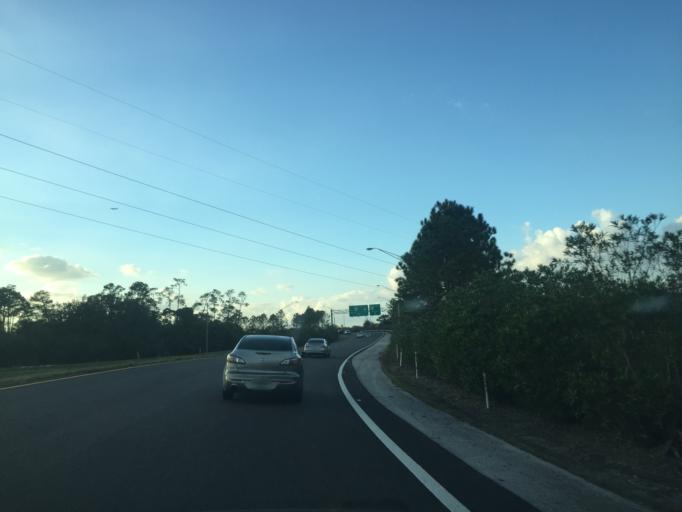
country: US
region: Florida
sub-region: Orange County
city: Union Park
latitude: 28.5481
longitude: -81.2557
